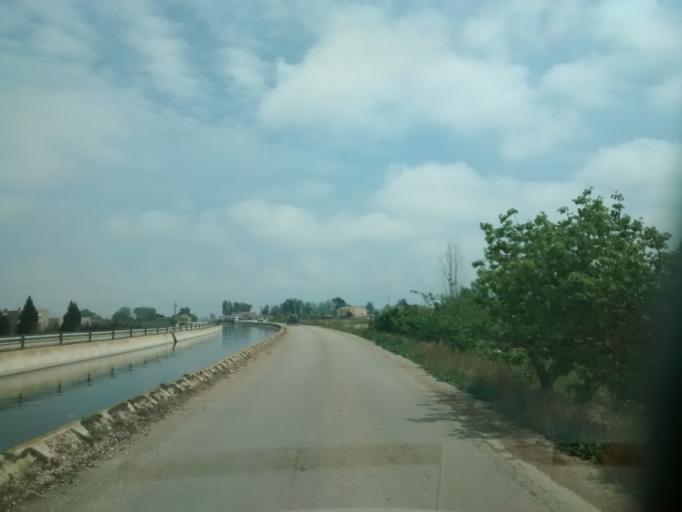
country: ES
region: Catalonia
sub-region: Provincia de Tarragona
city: Deltebre
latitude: 40.7022
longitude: 0.7270
